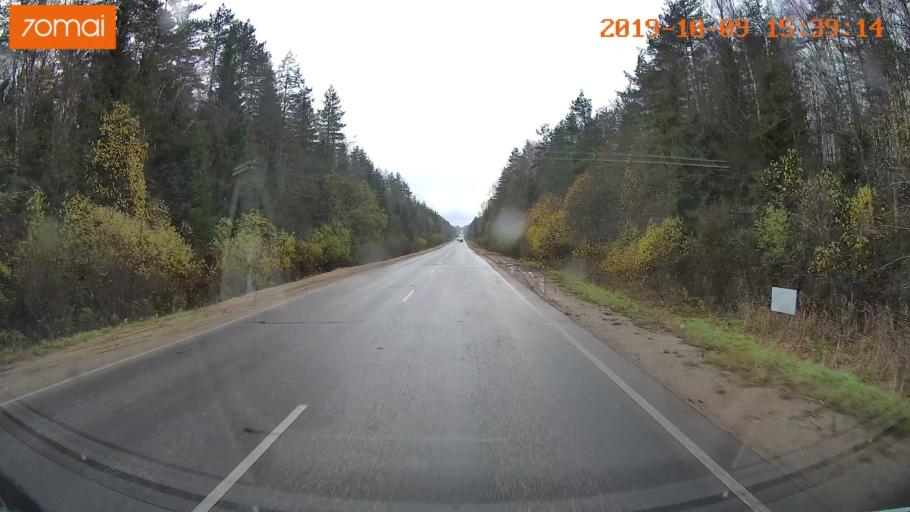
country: RU
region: Kostroma
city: Oktyabr'skiy
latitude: 57.8991
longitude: 41.1690
